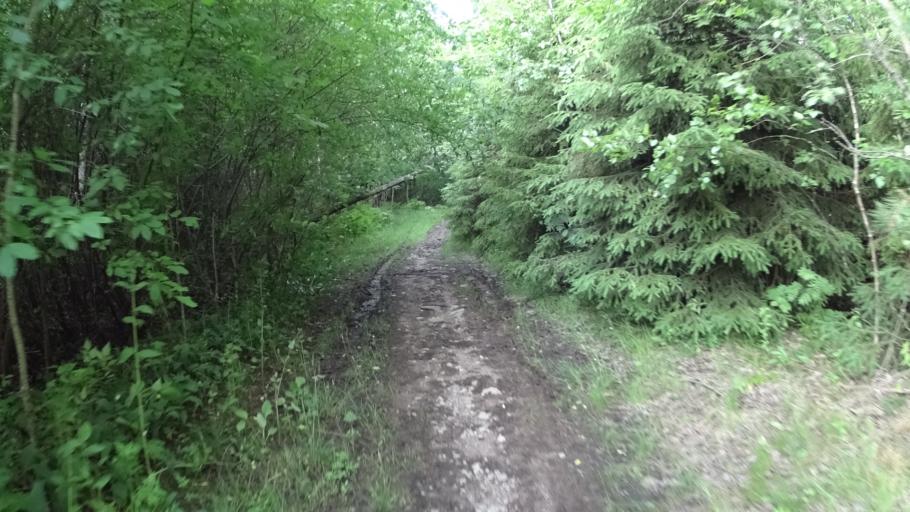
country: FI
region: Uusimaa
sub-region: Helsinki
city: Kilo
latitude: 60.2832
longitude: 24.8037
